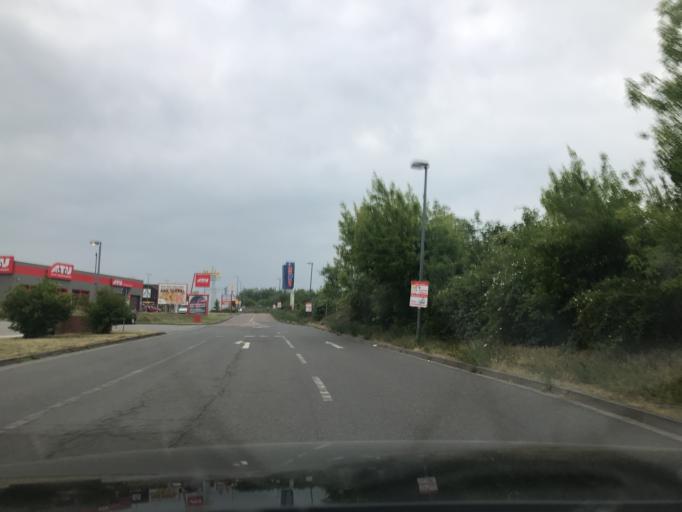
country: DE
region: Saxony-Anhalt
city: Angersdorf
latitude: 51.4644
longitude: 11.9111
